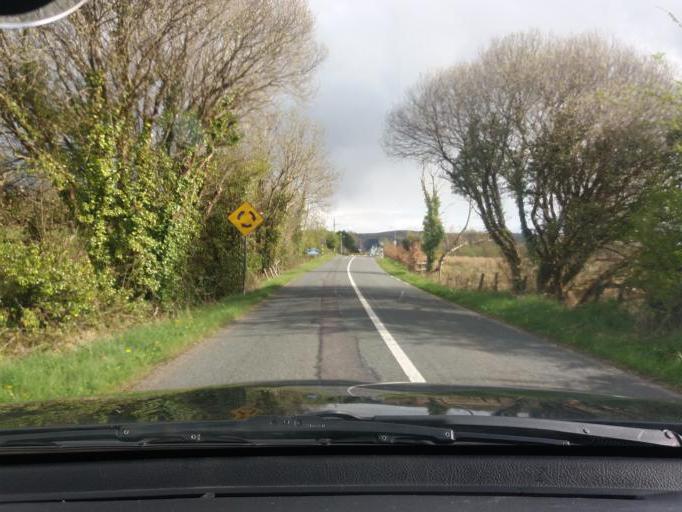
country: IE
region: Connaught
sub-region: County Leitrim
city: Manorhamilton
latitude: 54.3102
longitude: -8.1853
